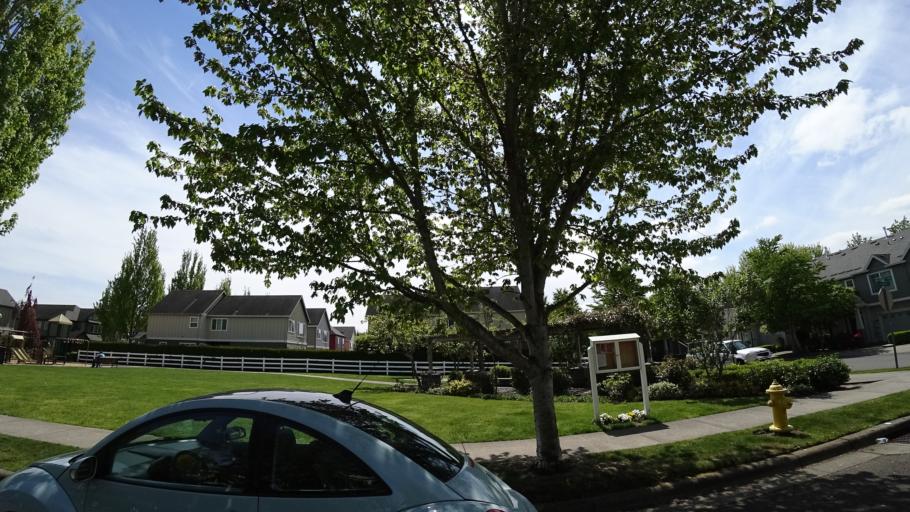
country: US
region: Oregon
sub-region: Washington County
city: Aloha
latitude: 45.4752
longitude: -122.8928
